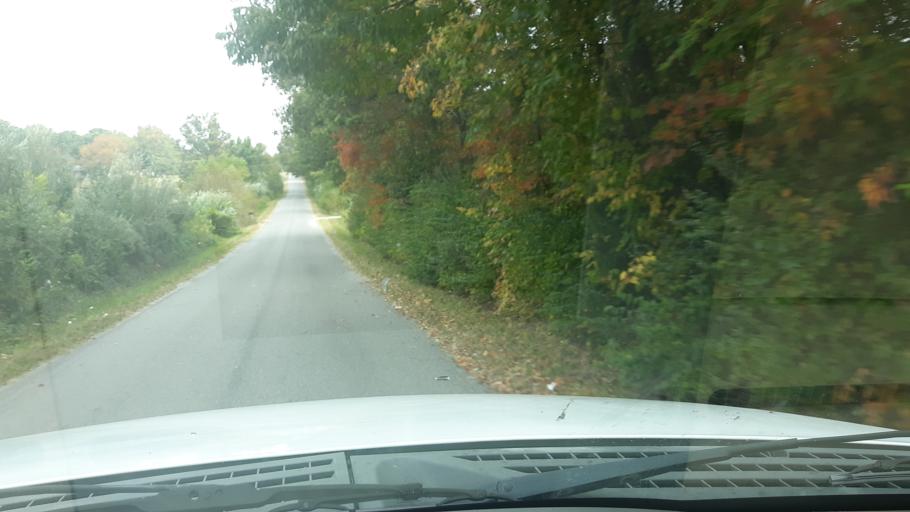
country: US
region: Illinois
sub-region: Saline County
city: Eldorado
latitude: 37.8304
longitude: -88.4848
